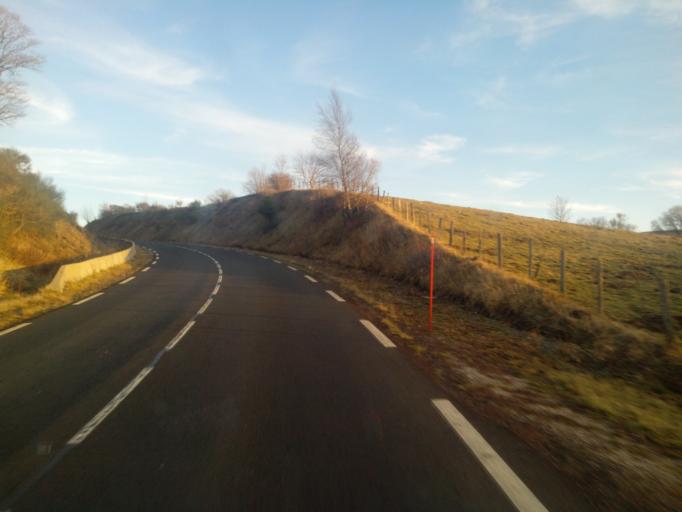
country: FR
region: Auvergne
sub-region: Departement du Cantal
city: Riom-es-Montagnes
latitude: 45.2351
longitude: 2.7464
